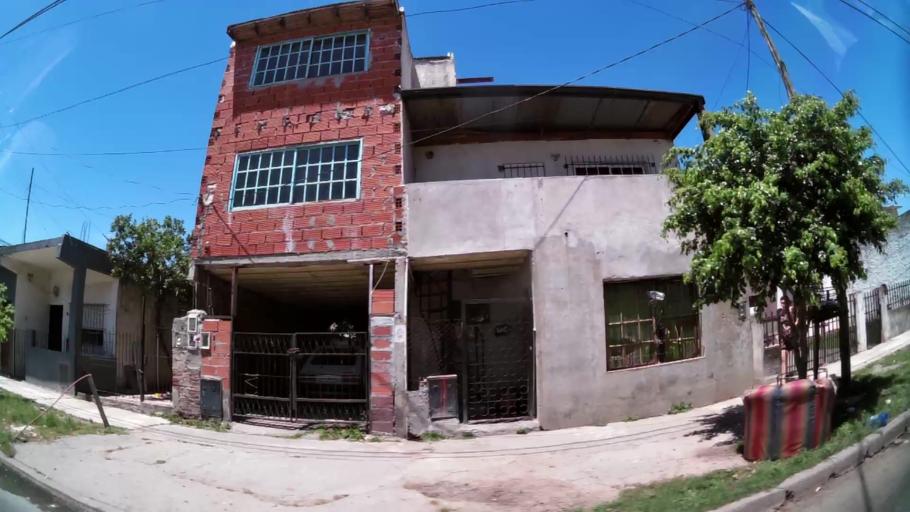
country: AR
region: Buenos Aires
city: Hurlingham
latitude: -34.5064
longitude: -58.7072
